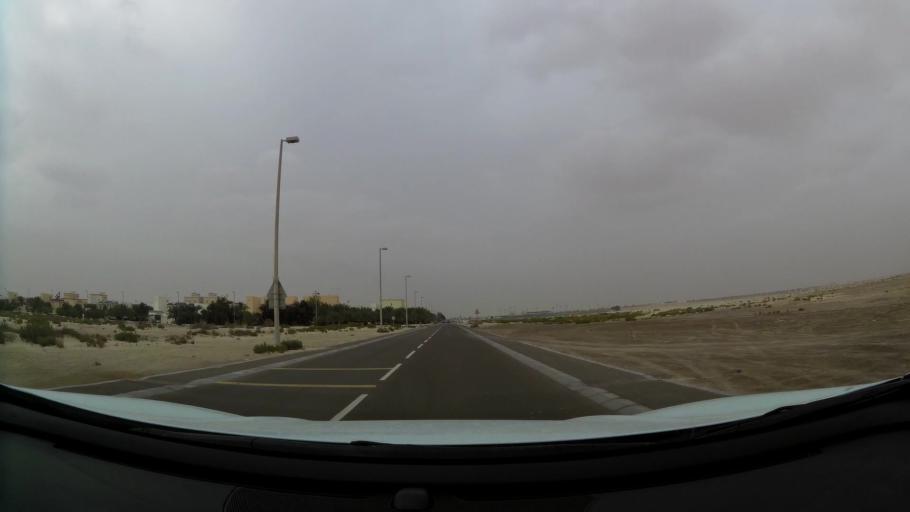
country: AE
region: Abu Dhabi
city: Abu Dhabi
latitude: 24.3762
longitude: 54.6738
